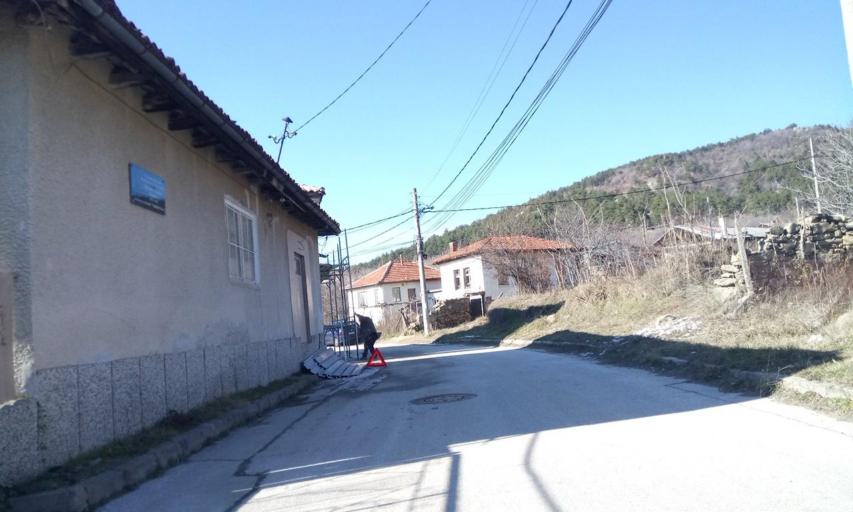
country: BG
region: Plovdiv
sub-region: Obshtina Khisarya
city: Khisarya
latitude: 42.5232
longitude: 24.7210
